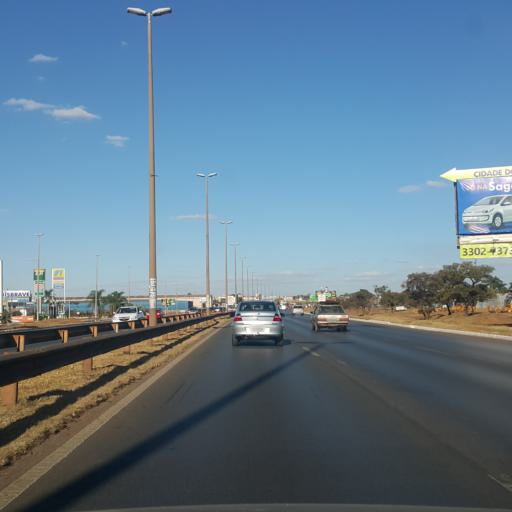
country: BR
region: Federal District
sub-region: Brasilia
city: Brasilia
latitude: -15.7878
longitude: -47.9876
